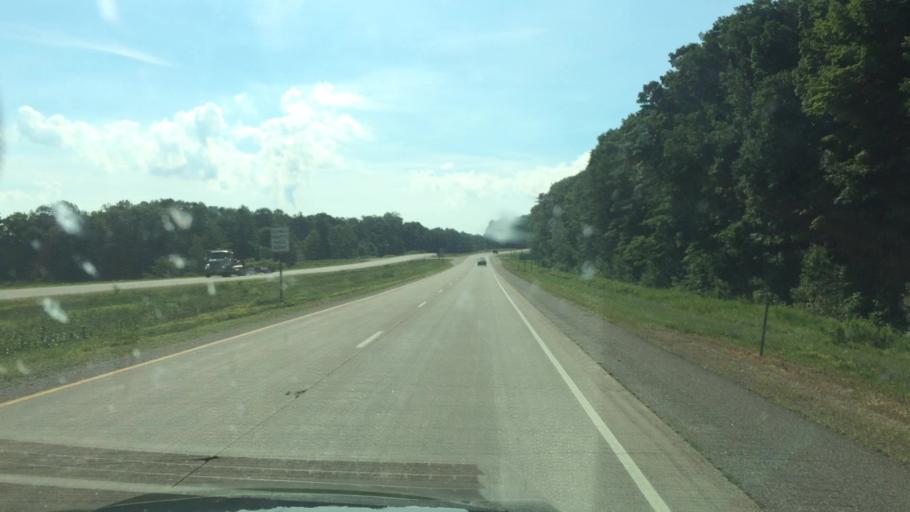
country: US
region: Wisconsin
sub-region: Shawano County
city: Wittenberg
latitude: 44.8253
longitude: -89.0666
